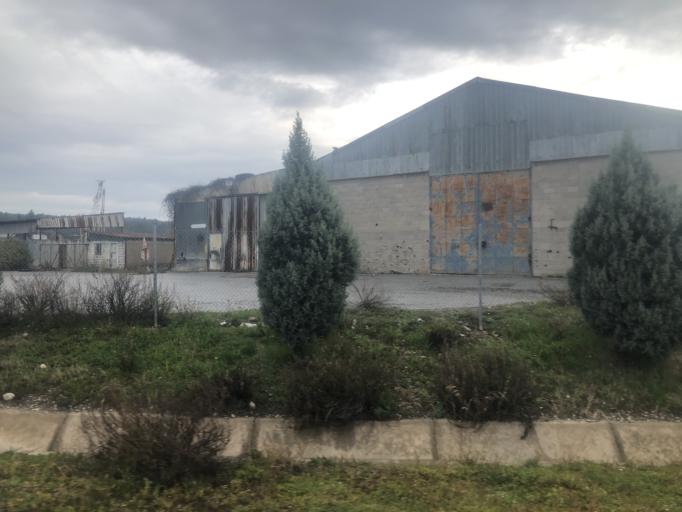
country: TR
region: Izmir
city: Buca
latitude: 38.3677
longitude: 27.2191
